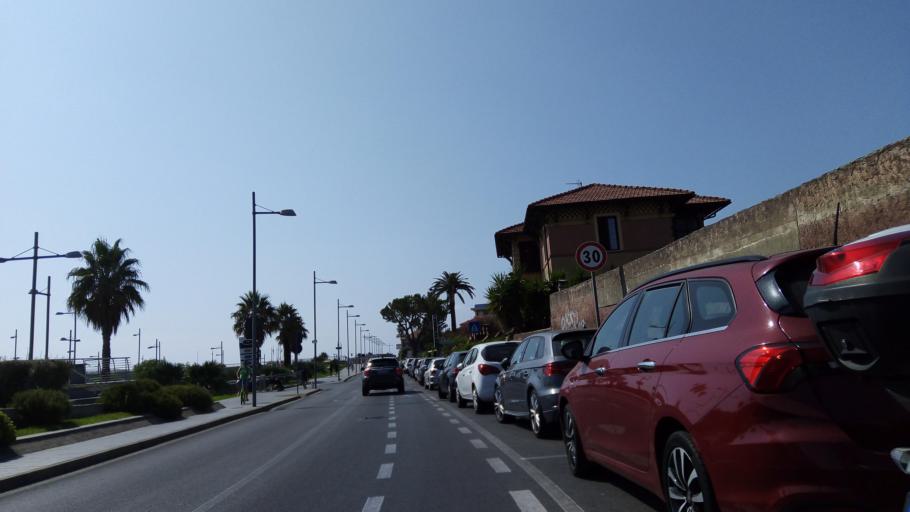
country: IT
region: Liguria
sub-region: Provincia di Savona
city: Loano
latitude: 44.1321
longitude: 8.2626
